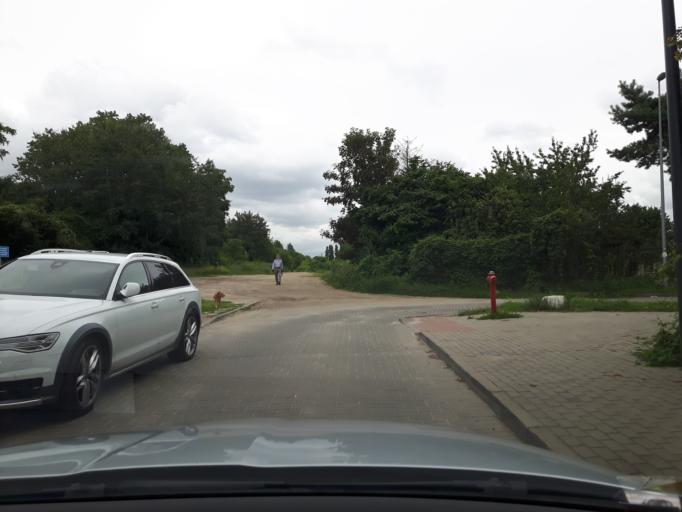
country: PL
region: Pomeranian Voivodeship
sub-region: Sopot
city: Sopot
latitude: 54.4303
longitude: 18.5776
